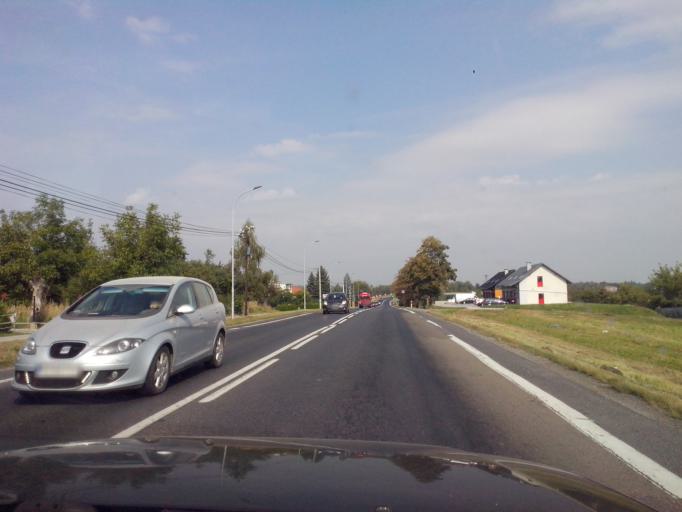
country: PL
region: Subcarpathian Voivodeship
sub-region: Powiat rzeszowski
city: Lutoryz
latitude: 49.9685
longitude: 21.9217
